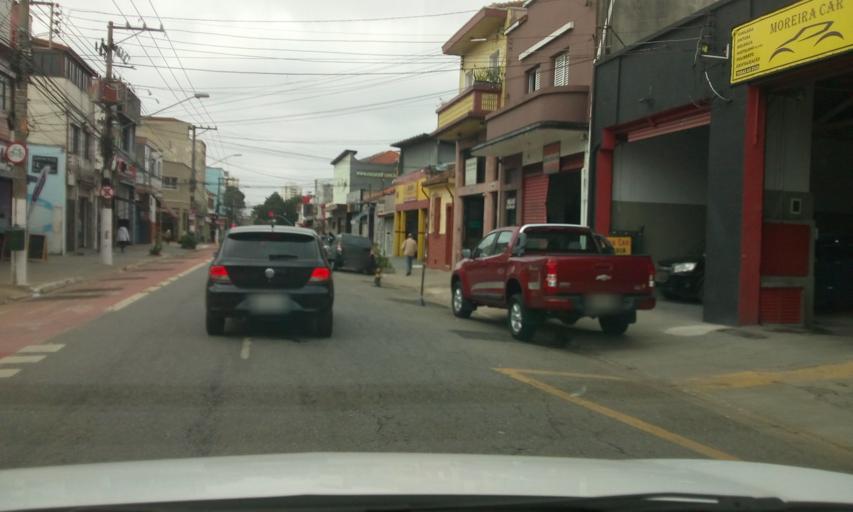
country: BR
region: Sao Paulo
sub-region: Sao Paulo
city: Sao Paulo
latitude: -23.5532
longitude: -46.5847
